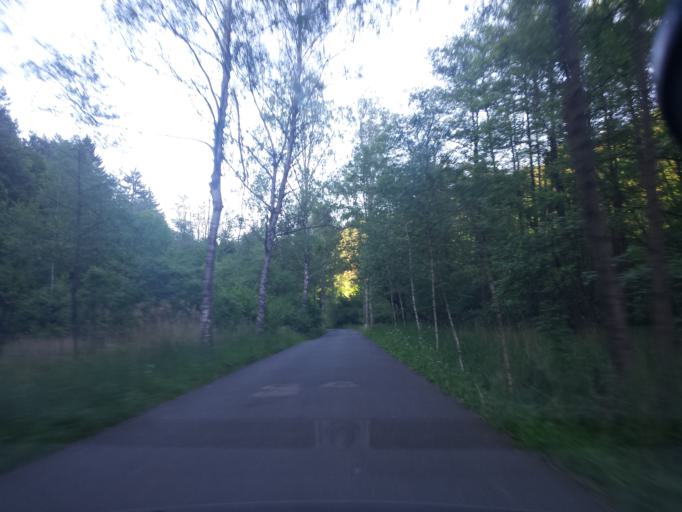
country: CZ
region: Central Bohemia
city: Mseno
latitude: 50.4510
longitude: 14.5833
